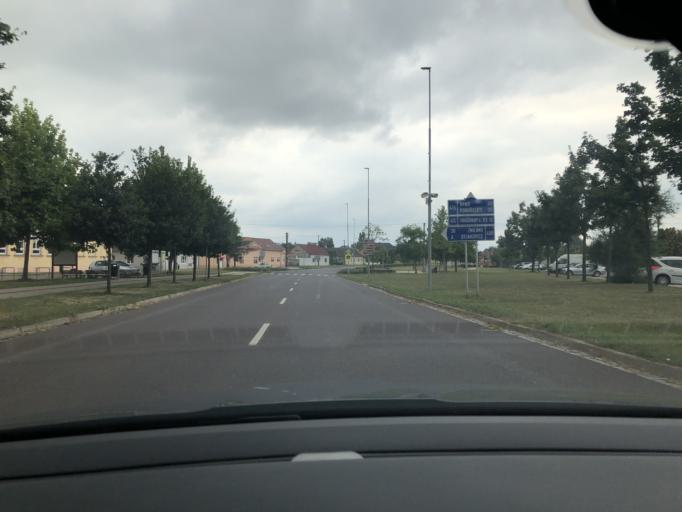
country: CZ
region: South Moravian
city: Hevlin
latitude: 48.7514
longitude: 16.3807
